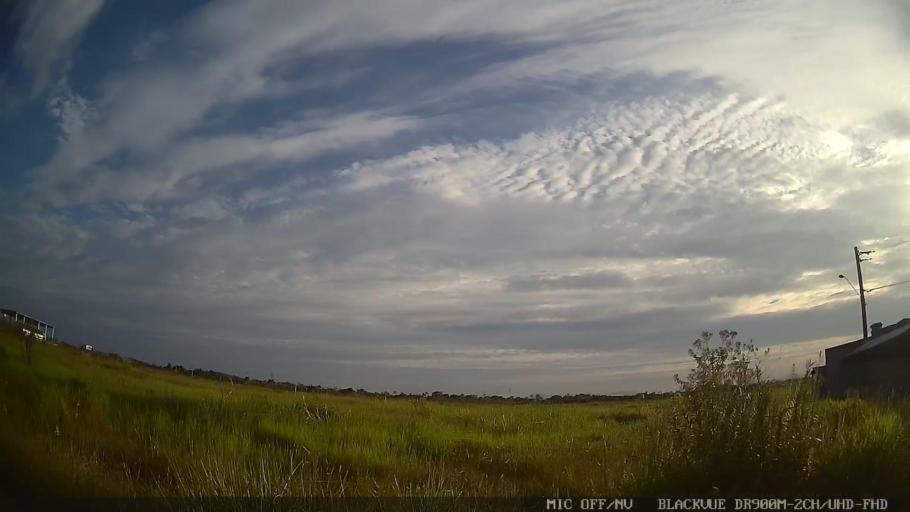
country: BR
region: Sao Paulo
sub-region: Itanhaem
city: Itanhaem
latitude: -24.1549
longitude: -46.7906
